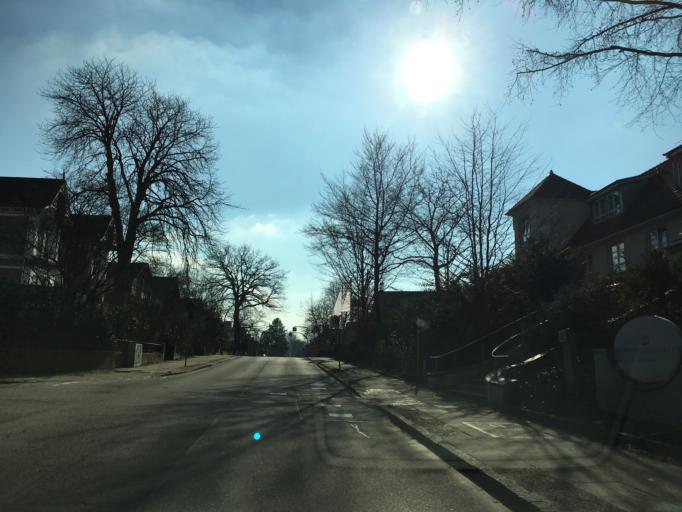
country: DE
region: Hamburg
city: Eidelstedt
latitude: 53.5581
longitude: 9.8649
